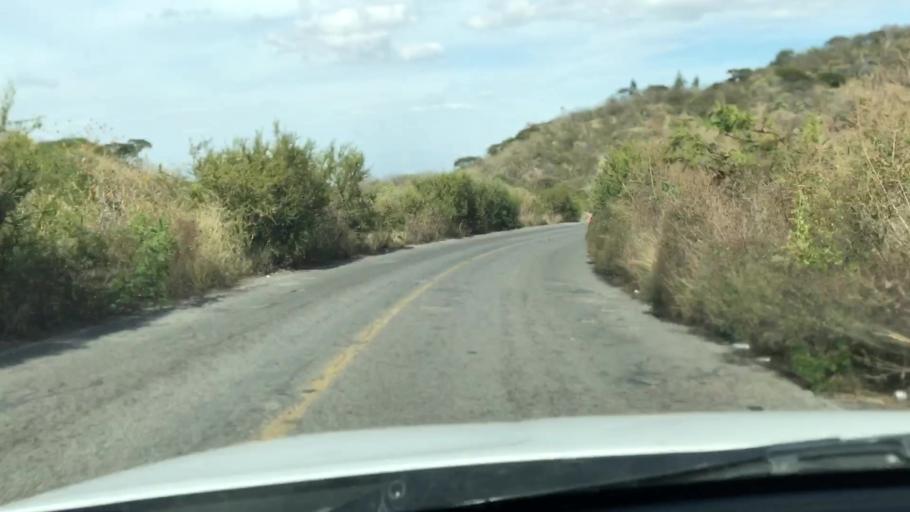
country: MX
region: Jalisco
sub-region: Zacoalco de Torres
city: Barranca de Otates (Barranca de Otatan)
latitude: 20.2461
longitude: -103.6782
